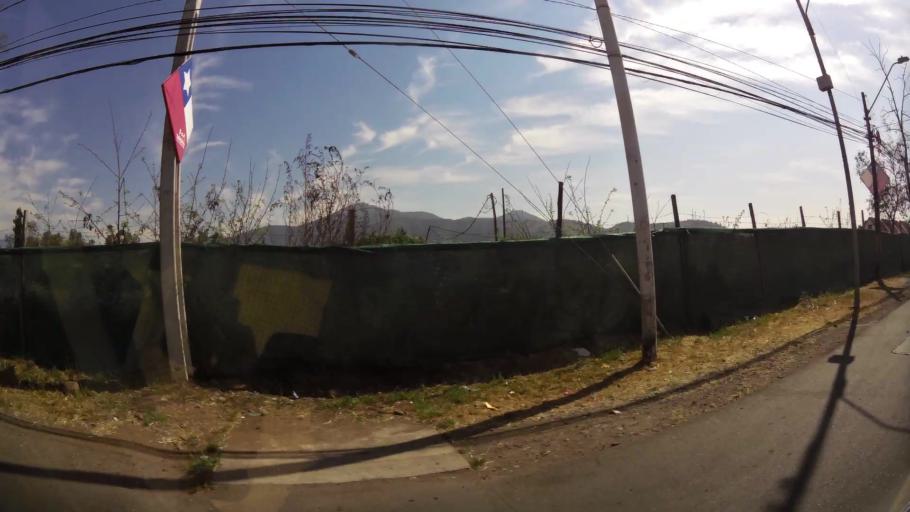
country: CL
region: Santiago Metropolitan
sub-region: Provincia de Talagante
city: Talagante
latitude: -33.6728
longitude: -70.9468
